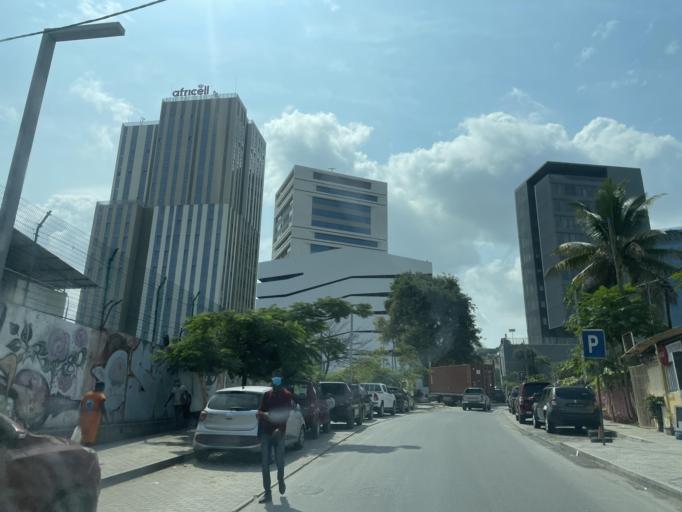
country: AO
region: Luanda
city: Luanda
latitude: -8.8076
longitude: 13.2418
